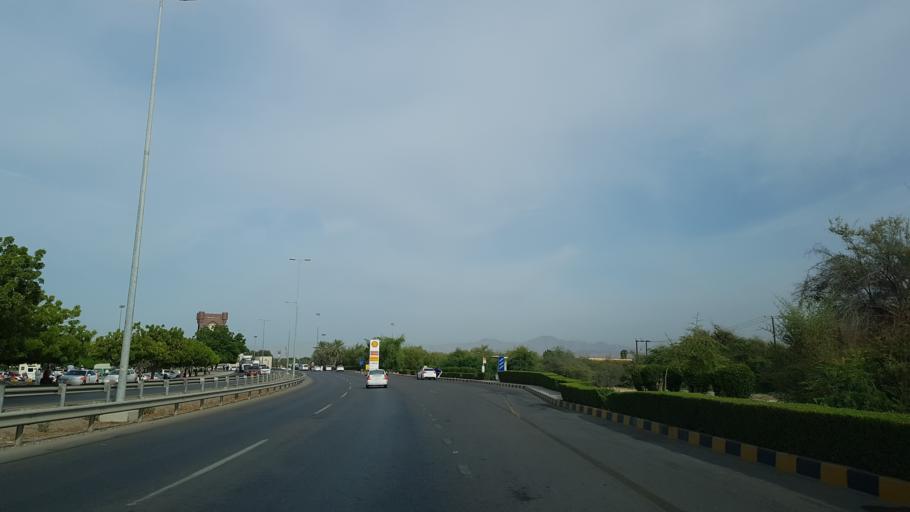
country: OM
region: Muhafazat Masqat
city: As Sib al Jadidah
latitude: 23.5876
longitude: 58.2475
